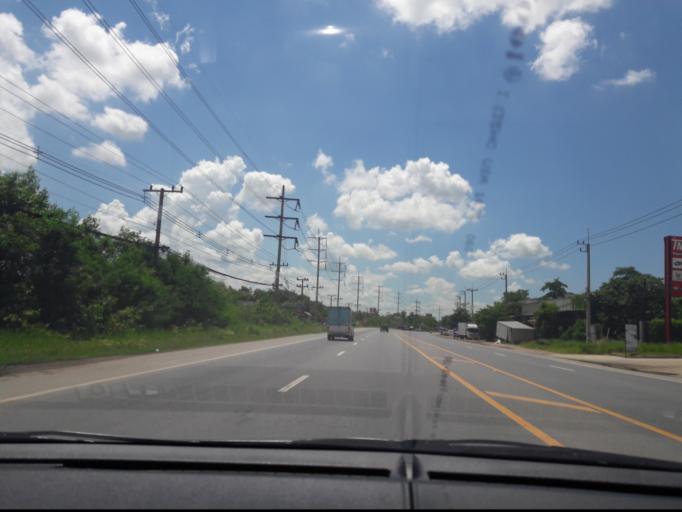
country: TH
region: Nakhon Pathom
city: Kamphaeng Saen
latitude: 14.0105
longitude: 100.0062
